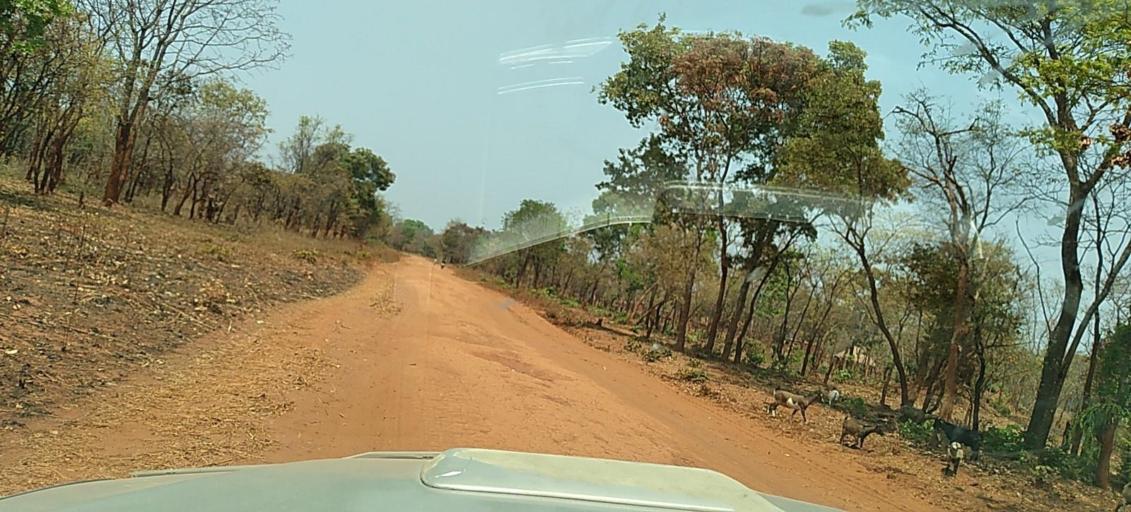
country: ZM
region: North-Western
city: Kasempa
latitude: -13.6250
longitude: 26.2134
